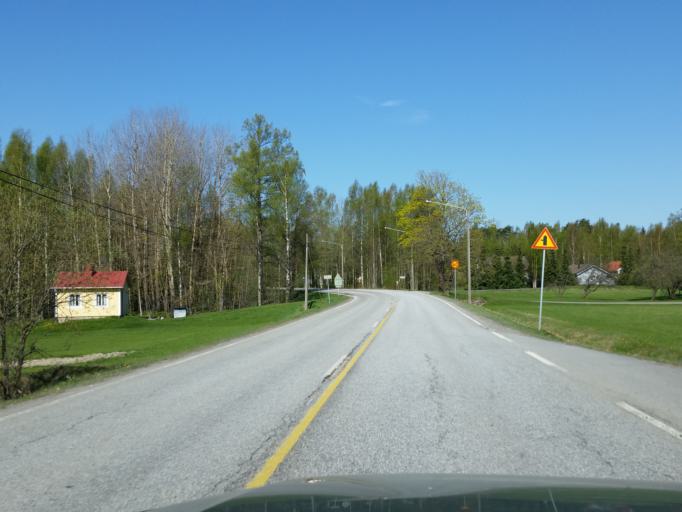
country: FI
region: Uusimaa
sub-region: Helsinki
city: Lohja
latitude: 60.1732
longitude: 24.1266
